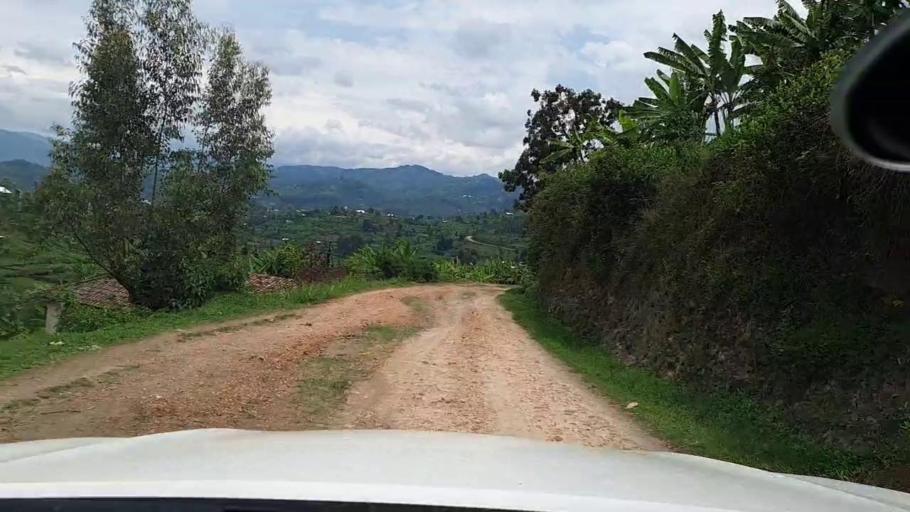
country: RW
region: Western Province
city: Kibuye
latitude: -2.0821
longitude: 29.4181
